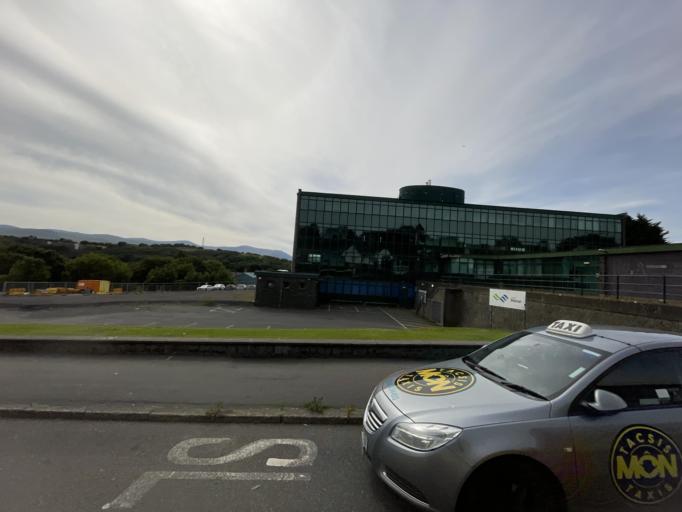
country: GB
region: Wales
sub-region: Gwynedd
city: Bangor
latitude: 53.2240
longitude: -4.1414
